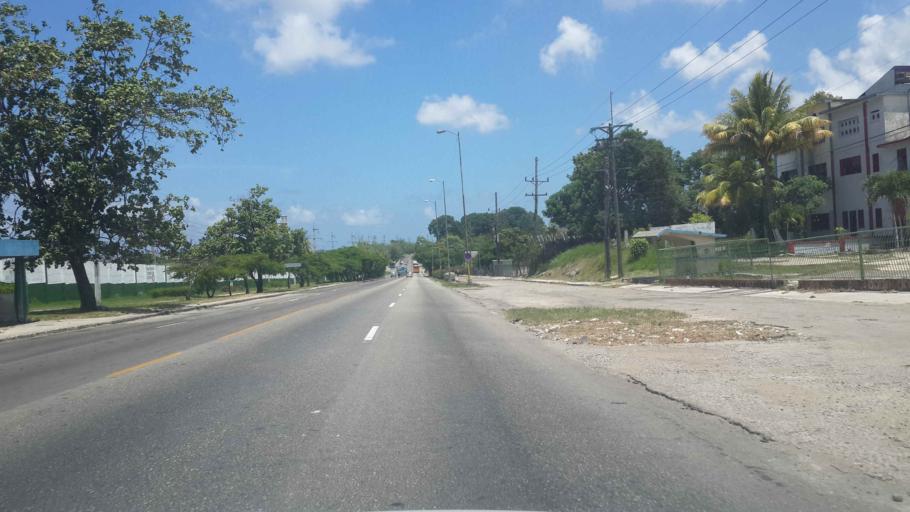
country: CU
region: La Habana
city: Guanabacoa
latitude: 23.1289
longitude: -82.3154
